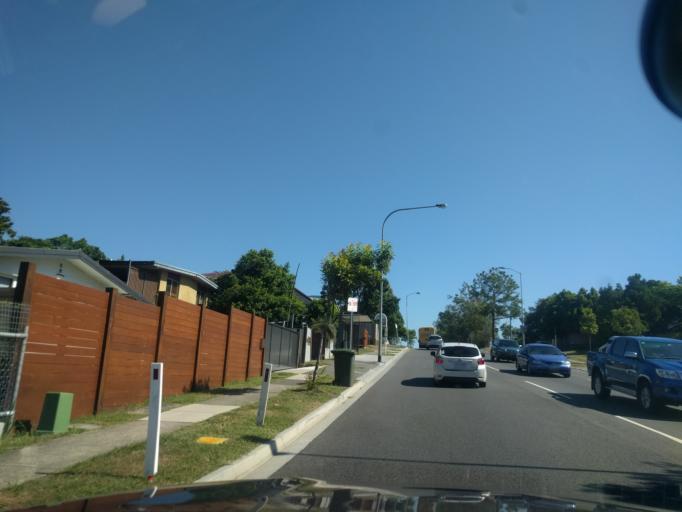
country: AU
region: Queensland
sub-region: Brisbane
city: Stafford Heights
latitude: -27.4006
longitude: 153.0095
